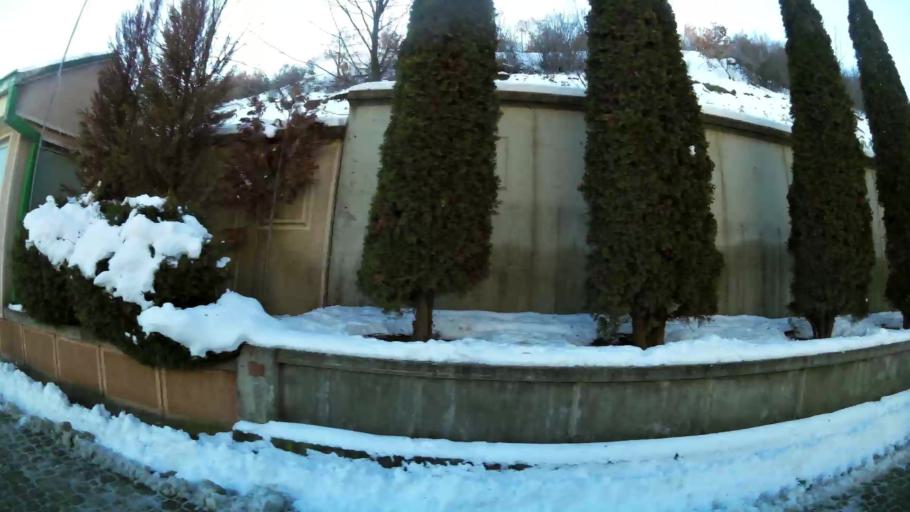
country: MK
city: Ljubin
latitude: 42.0029
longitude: 21.3004
